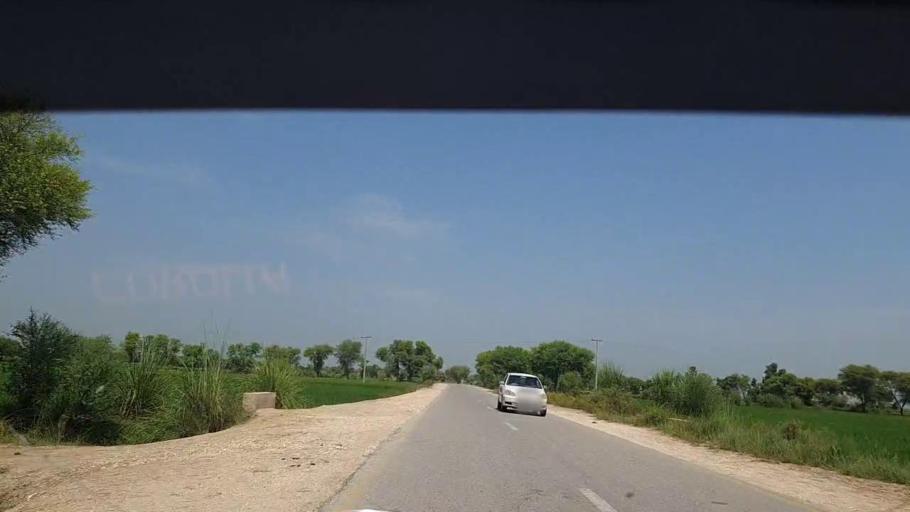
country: PK
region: Sindh
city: Thul
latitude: 28.1411
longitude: 68.8176
